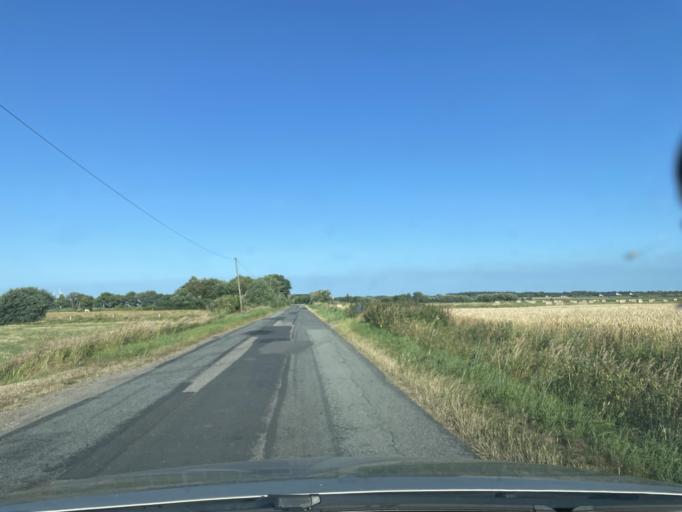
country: DE
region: Schleswig-Holstein
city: Aventoft
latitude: 54.8772
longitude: 8.8331
